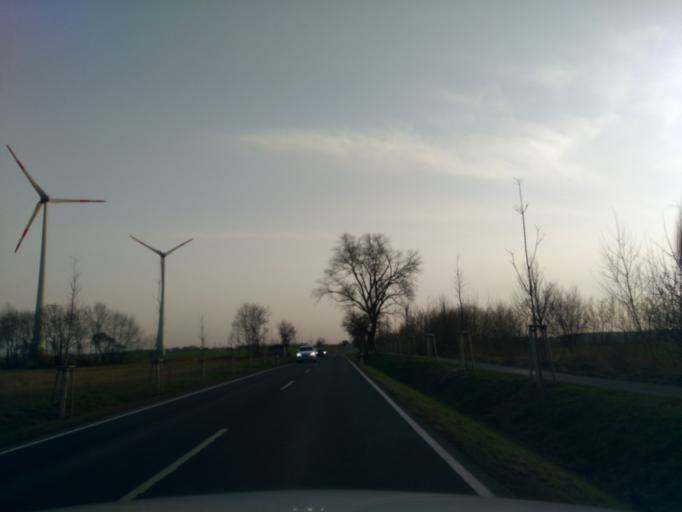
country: DE
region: Brandenburg
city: Velten
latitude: 52.6875
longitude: 13.1208
